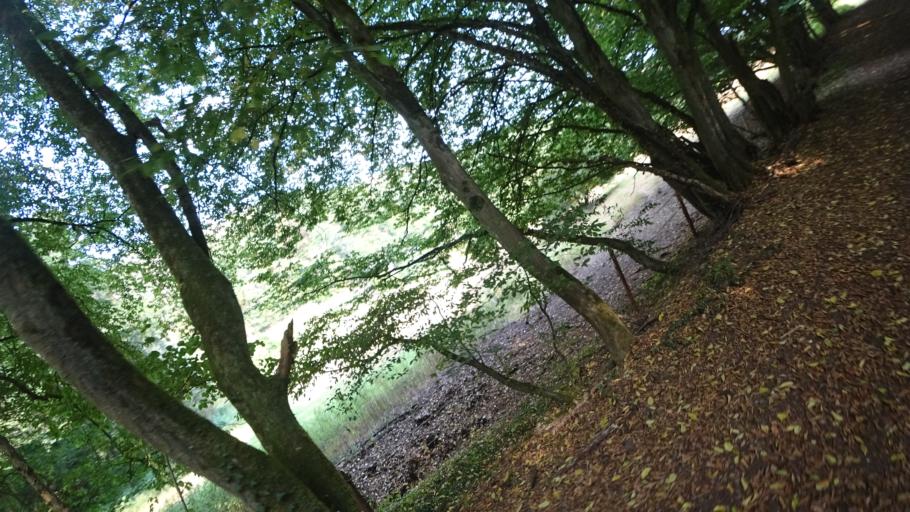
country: DE
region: Rheinland-Pfalz
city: Kammerforst
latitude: 50.4623
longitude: 7.6727
